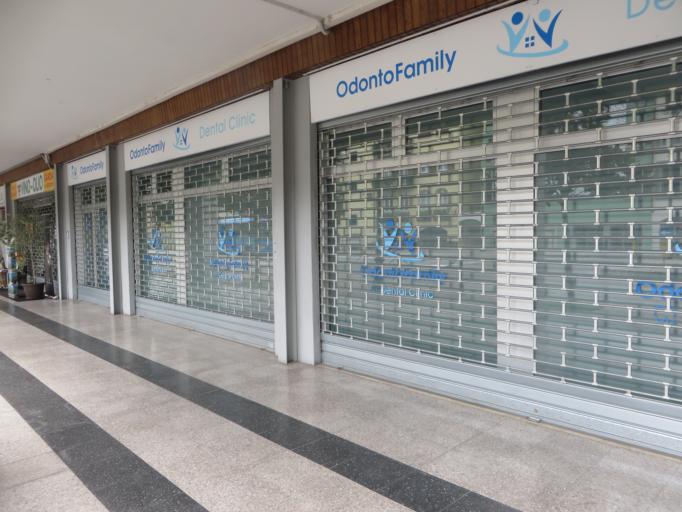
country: IT
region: Lombardy
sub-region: Provincia di Brescia
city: Salo
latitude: 45.6076
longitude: 10.5246
